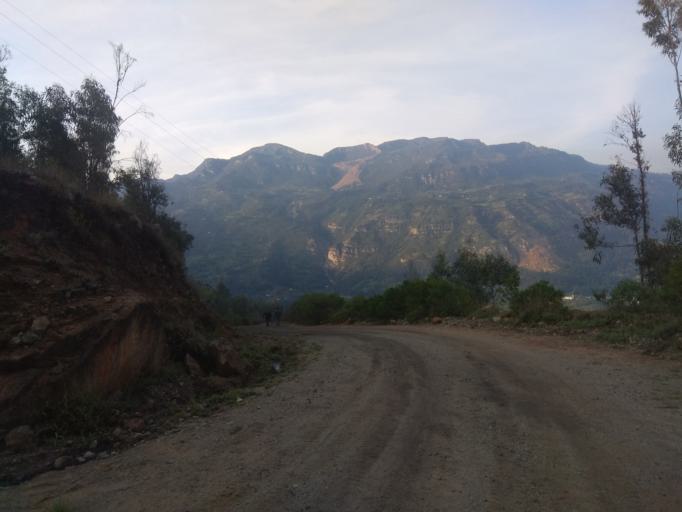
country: CO
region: Boyaca
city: Socha Viejo
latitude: 5.9944
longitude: -72.7007
